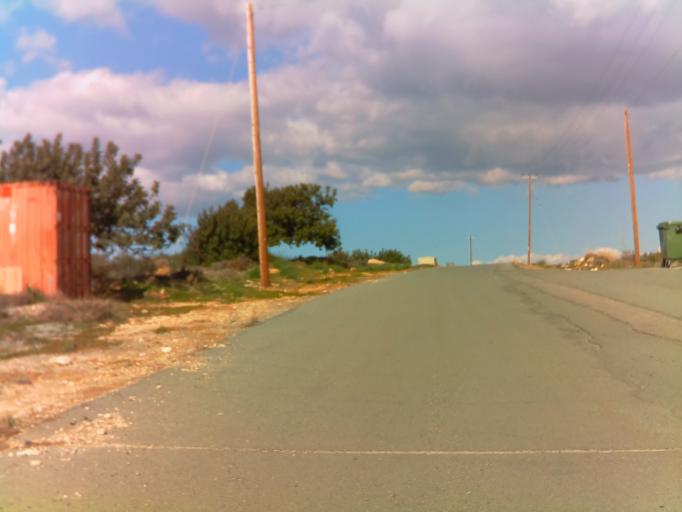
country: CY
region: Limassol
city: Pissouri
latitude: 34.6527
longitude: 32.6983
